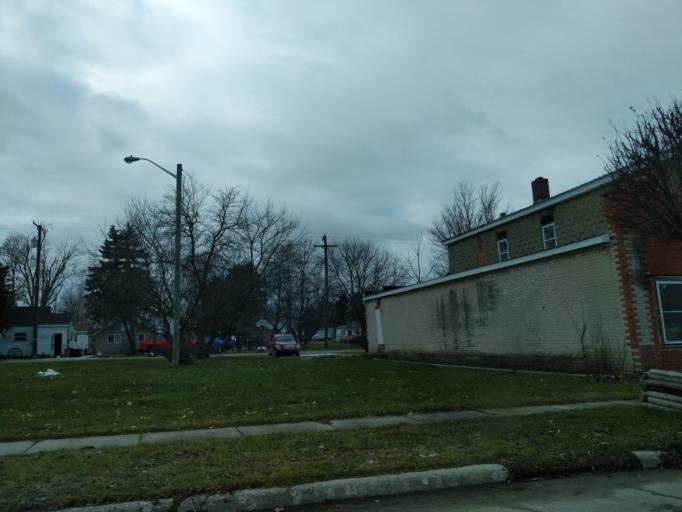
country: US
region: Michigan
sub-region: Lapeer County
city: North Branch
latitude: 43.3142
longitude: -83.1792
